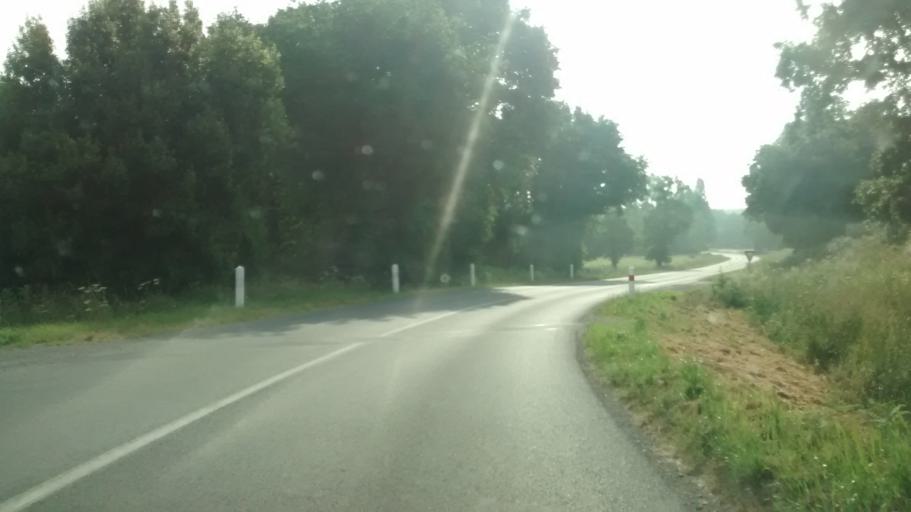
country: FR
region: Brittany
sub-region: Departement du Morbihan
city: Guer
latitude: 47.9027
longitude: -2.1413
